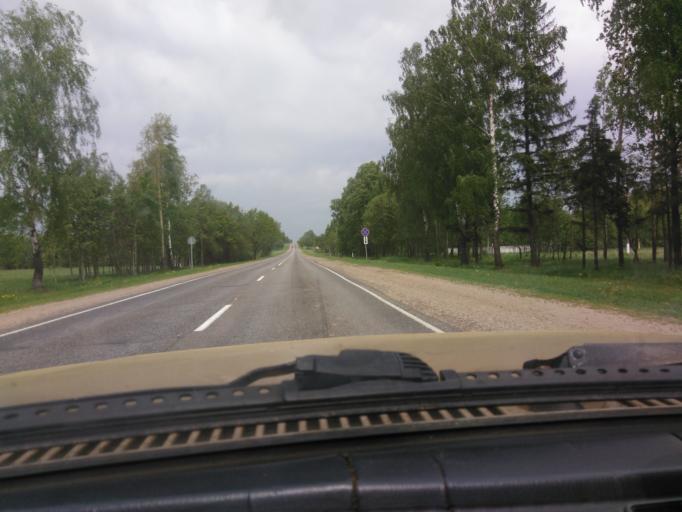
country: BY
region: Mogilev
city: Palykavichy Pyershyya
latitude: 54.0053
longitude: 30.3204
